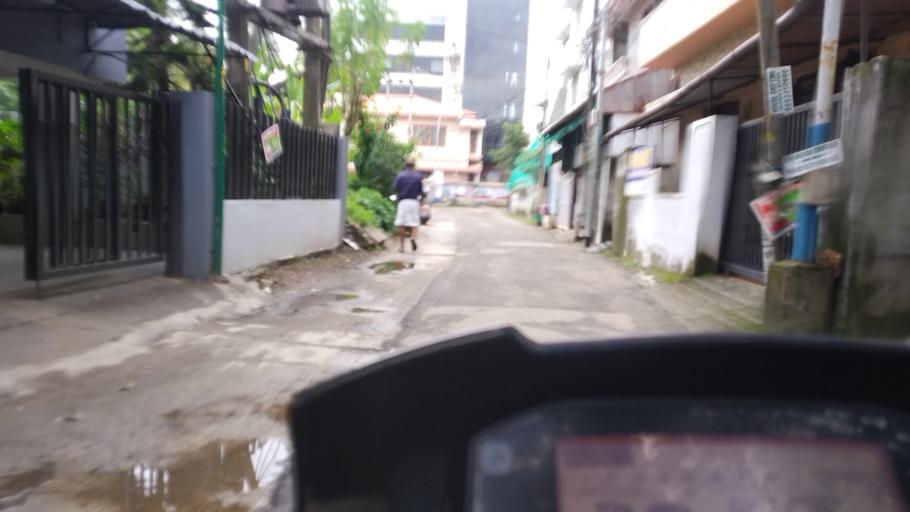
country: IN
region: Kerala
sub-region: Ernakulam
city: Cochin
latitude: 9.9727
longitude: 76.3103
